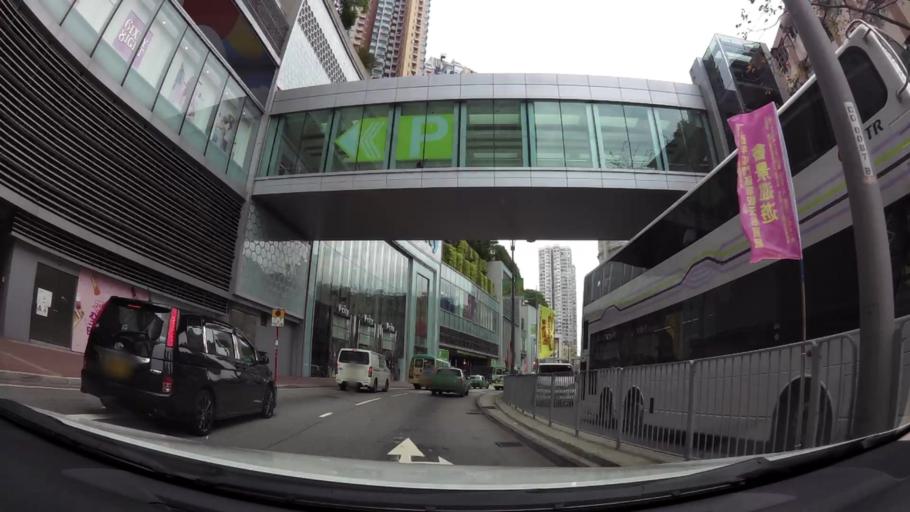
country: HK
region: Tuen Mun
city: Tuen Mun
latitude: 22.3952
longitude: 113.9744
